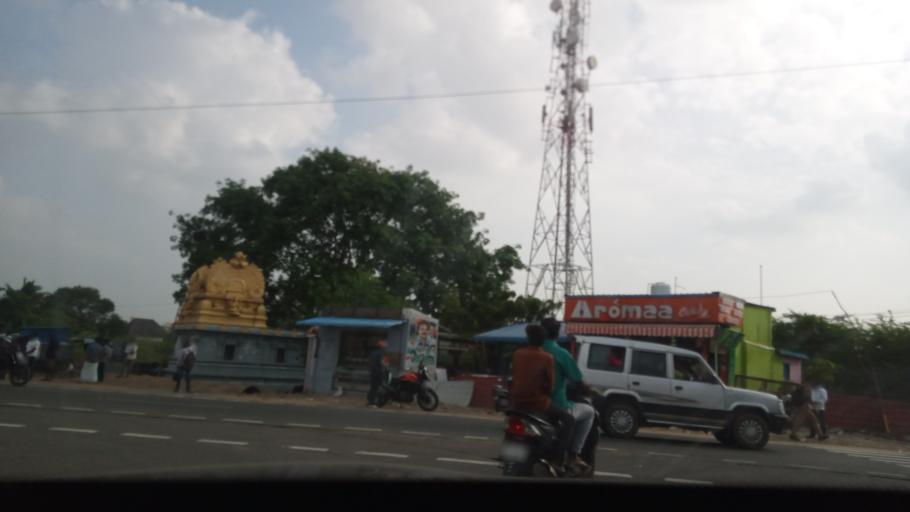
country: IN
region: Tamil Nadu
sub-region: Kancheepuram
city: Injambakkam
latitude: 12.7845
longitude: 80.2451
